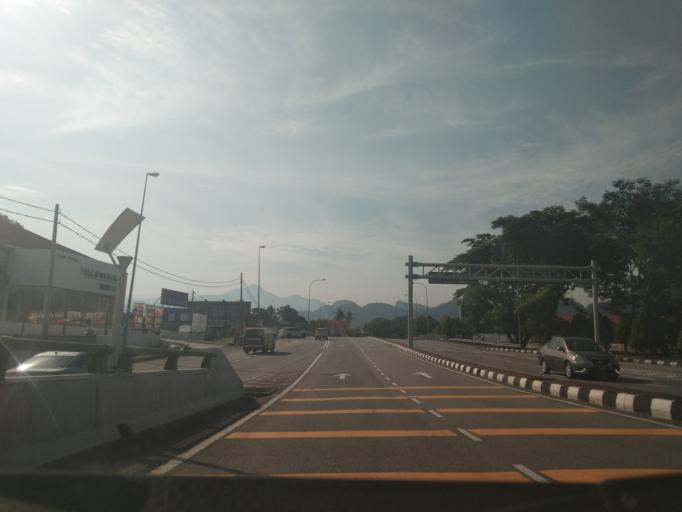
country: MY
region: Perak
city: Ipoh
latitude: 4.5768
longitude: 101.1080
